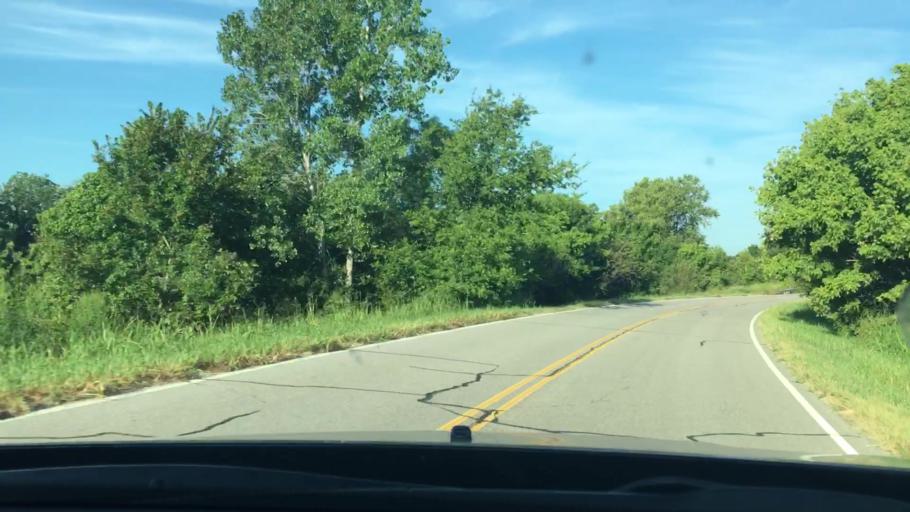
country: US
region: Oklahoma
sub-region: Pontotoc County
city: Ada
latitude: 34.6995
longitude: -96.4358
